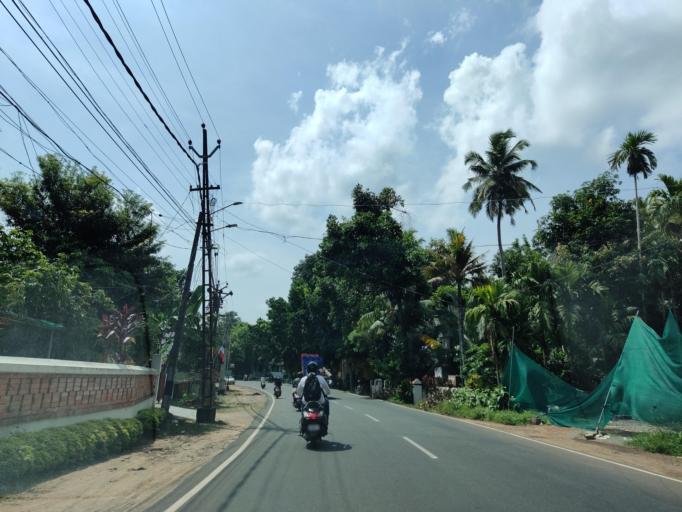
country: IN
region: Kerala
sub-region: Alappuzha
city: Mavelikara
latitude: 9.2611
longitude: 76.5441
